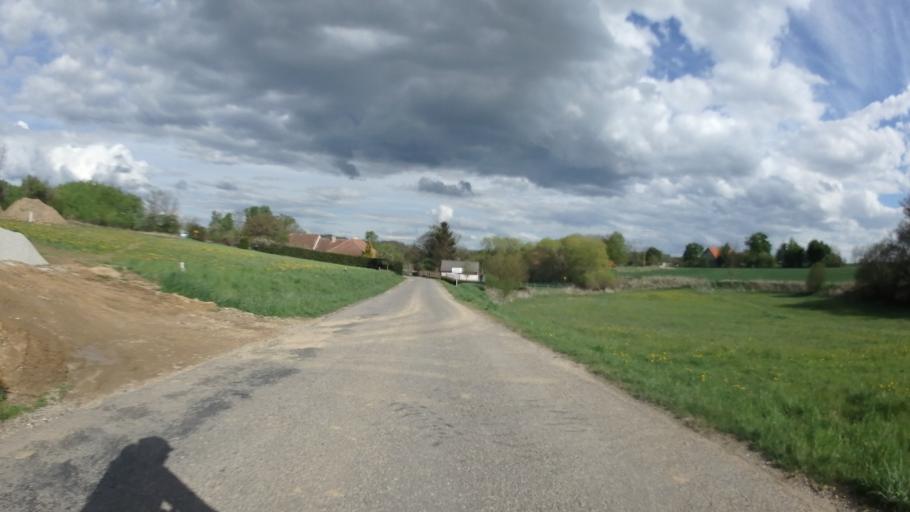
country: CZ
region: Vysocina
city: Merin
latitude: 49.3393
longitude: 15.8962
